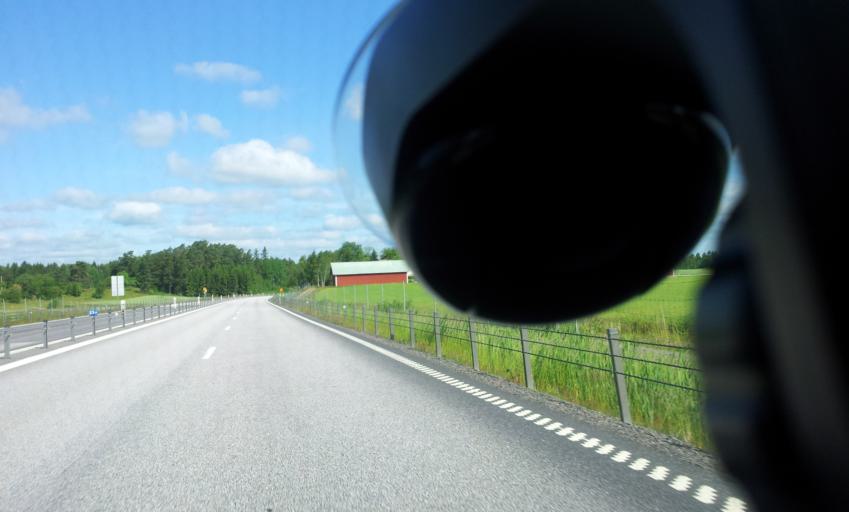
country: SE
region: OEstergoetland
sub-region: Valdemarsviks Kommun
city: Gusum
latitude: 58.3047
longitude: 16.4890
